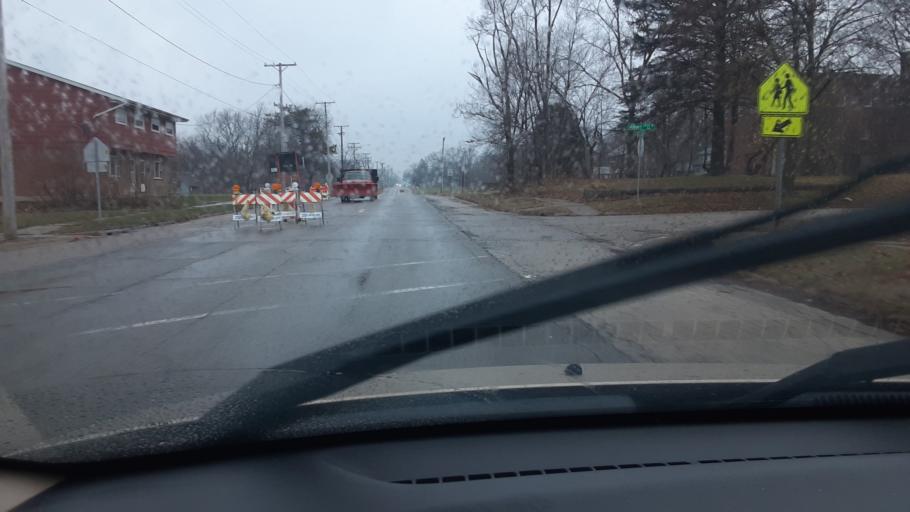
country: US
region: Illinois
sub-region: Winnebago County
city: Rockford
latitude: 42.2764
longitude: -89.1193
